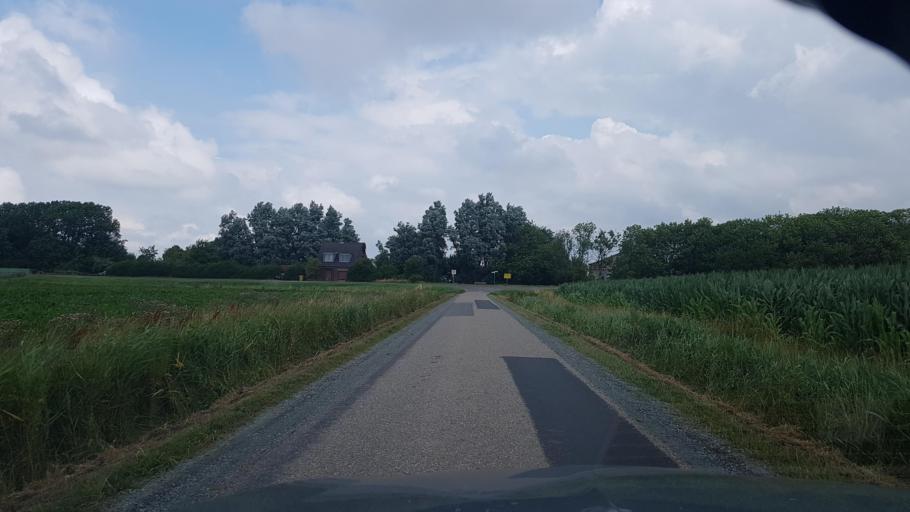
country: DE
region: Schleswig-Holstein
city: Elisabeth-Sophien-Koog
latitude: 54.5011
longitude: 8.8451
